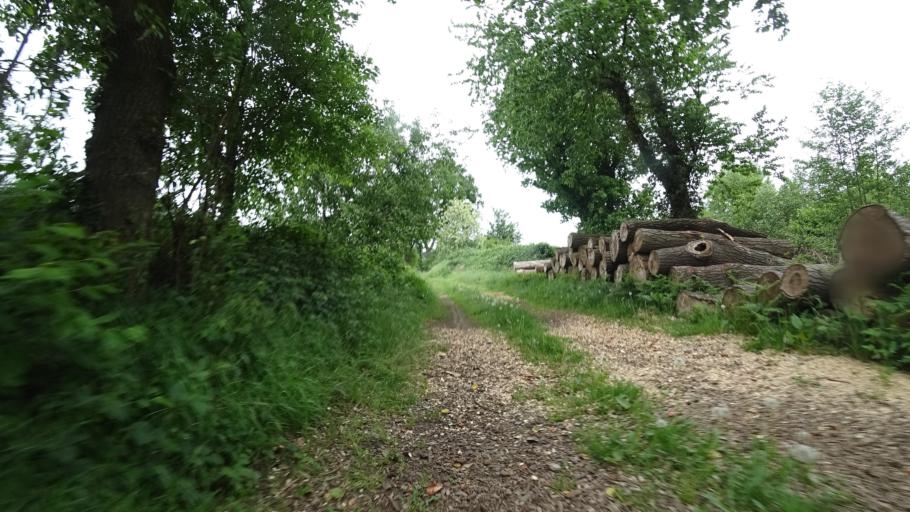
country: DE
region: North Rhine-Westphalia
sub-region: Regierungsbezirk Detmold
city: Rheda-Wiedenbruck
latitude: 51.8941
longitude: 8.3114
